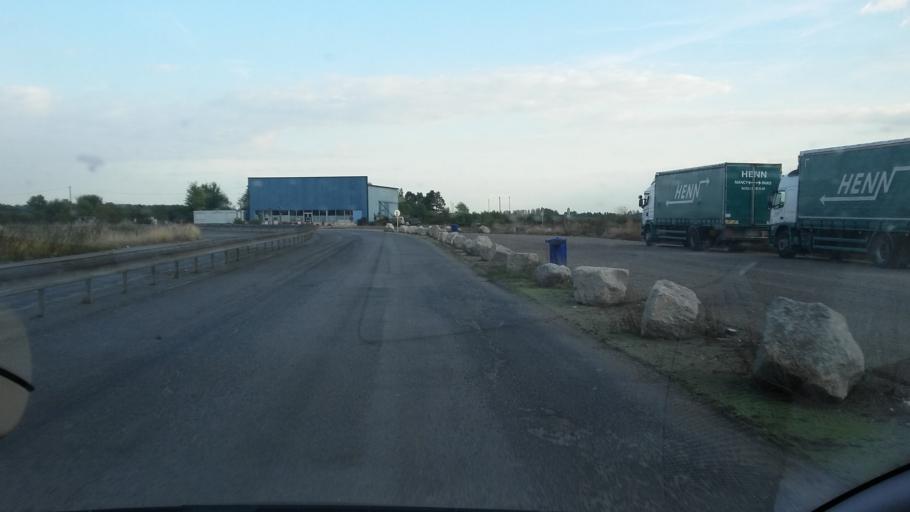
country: FR
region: Champagne-Ardenne
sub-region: Departement de la Marne
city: Connantre
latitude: 48.7243
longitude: 3.9000
